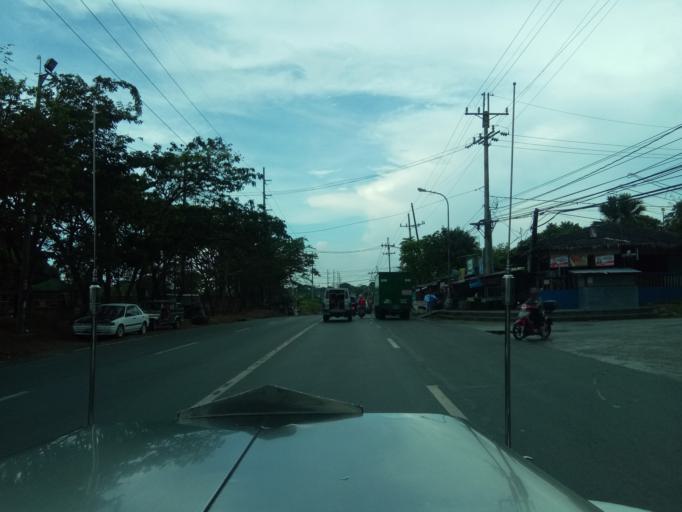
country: PH
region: Calabarzon
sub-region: Province of Cavite
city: Aliang
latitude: 14.2800
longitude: 120.8786
